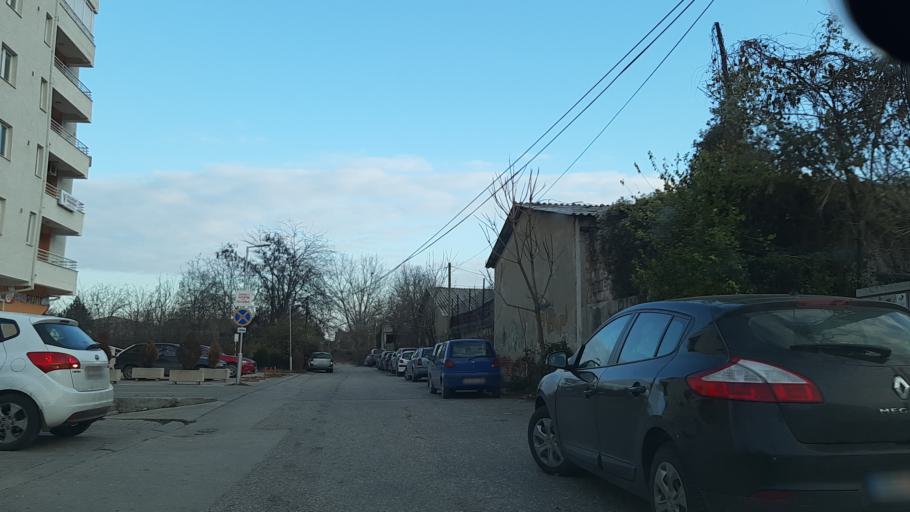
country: MK
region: Kisela Voda
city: Usje
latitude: 41.9788
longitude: 21.4489
